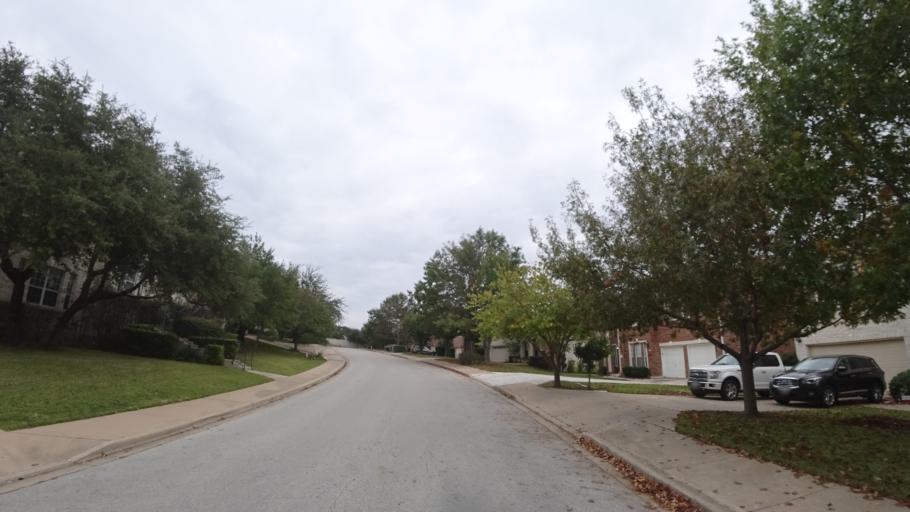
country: US
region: Texas
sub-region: Travis County
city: Bee Cave
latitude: 30.3128
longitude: -97.9195
